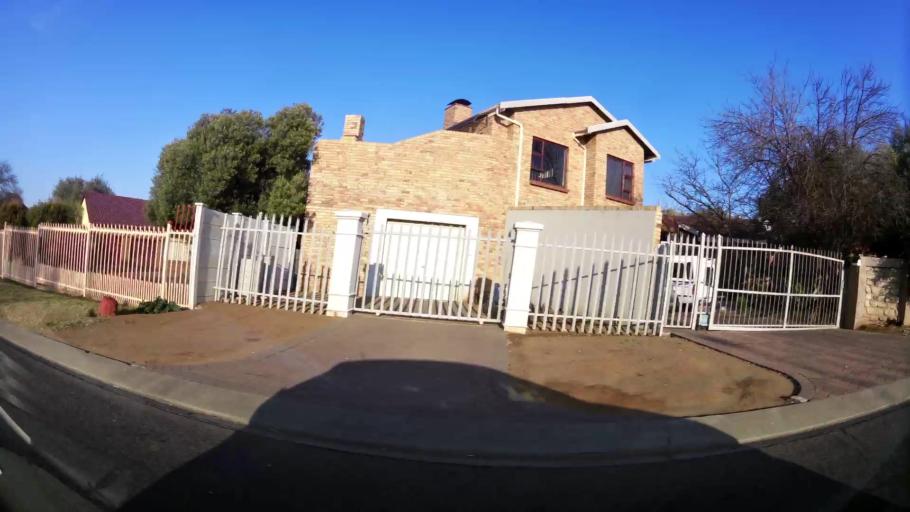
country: ZA
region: Orange Free State
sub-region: Mangaung Metropolitan Municipality
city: Bloemfontein
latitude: -29.1535
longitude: 26.1658
